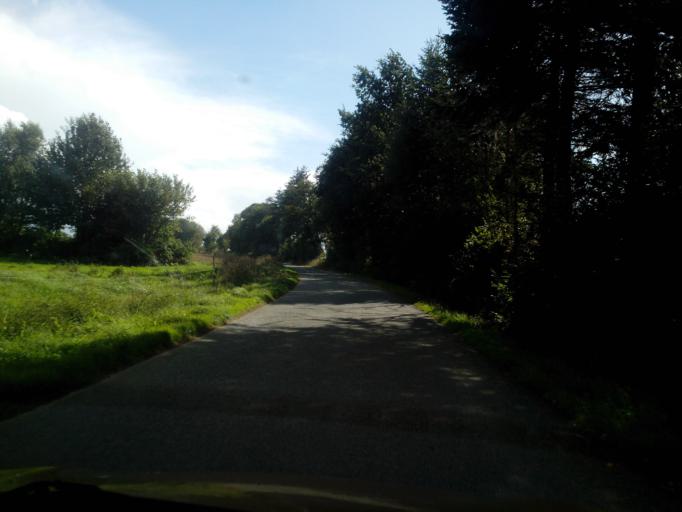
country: FR
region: Brittany
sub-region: Departement des Cotes-d'Armor
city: Merdrignac
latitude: 48.1706
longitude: -2.4198
